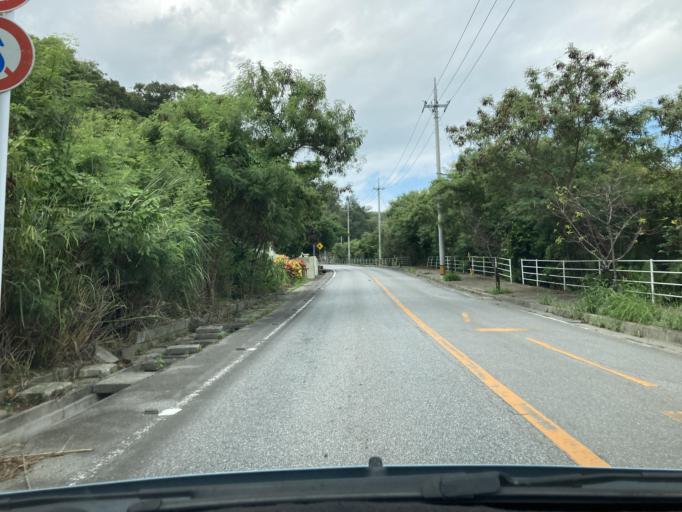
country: JP
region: Okinawa
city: Ginowan
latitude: 26.2601
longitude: 127.7849
